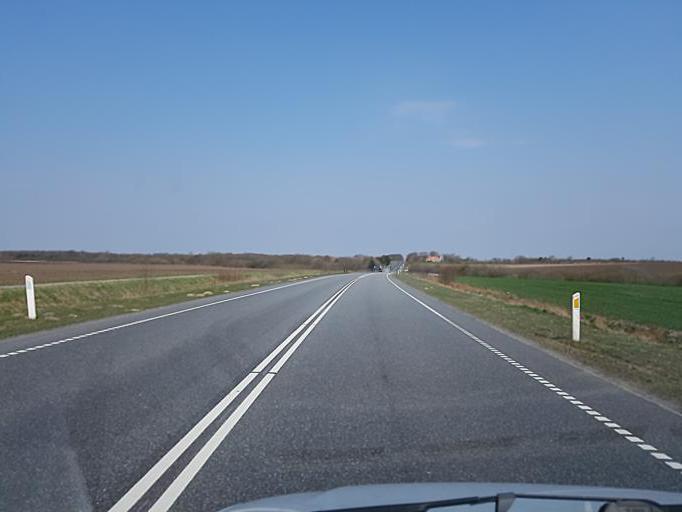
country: DK
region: South Denmark
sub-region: Varde Kommune
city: Varde
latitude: 55.6758
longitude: 8.4915
